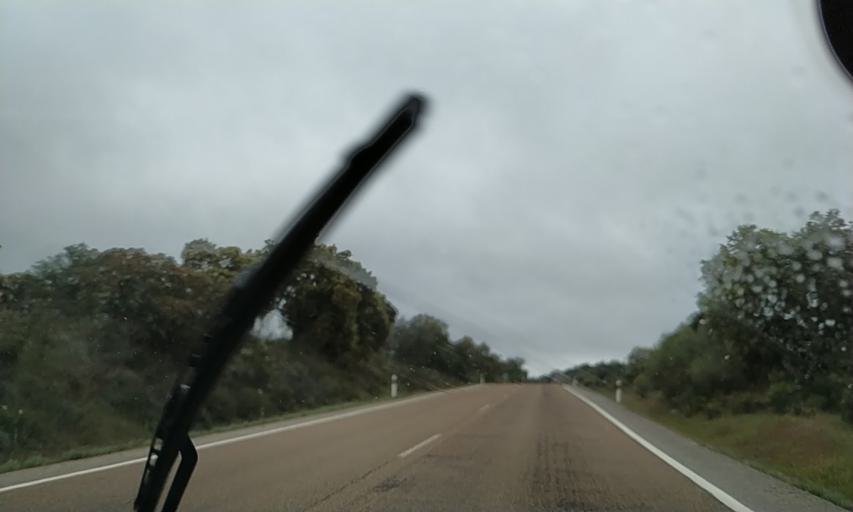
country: ES
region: Extremadura
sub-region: Provincia de Badajoz
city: Puebla de Obando
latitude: 39.2860
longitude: -6.5220
